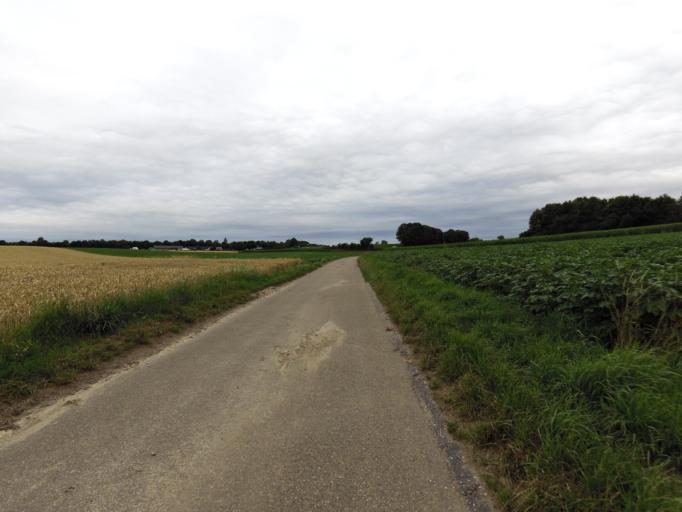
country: NL
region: Limburg
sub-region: Gemeente Kerkrade
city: Kerkrade
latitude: 50.9029
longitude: 6.0547
